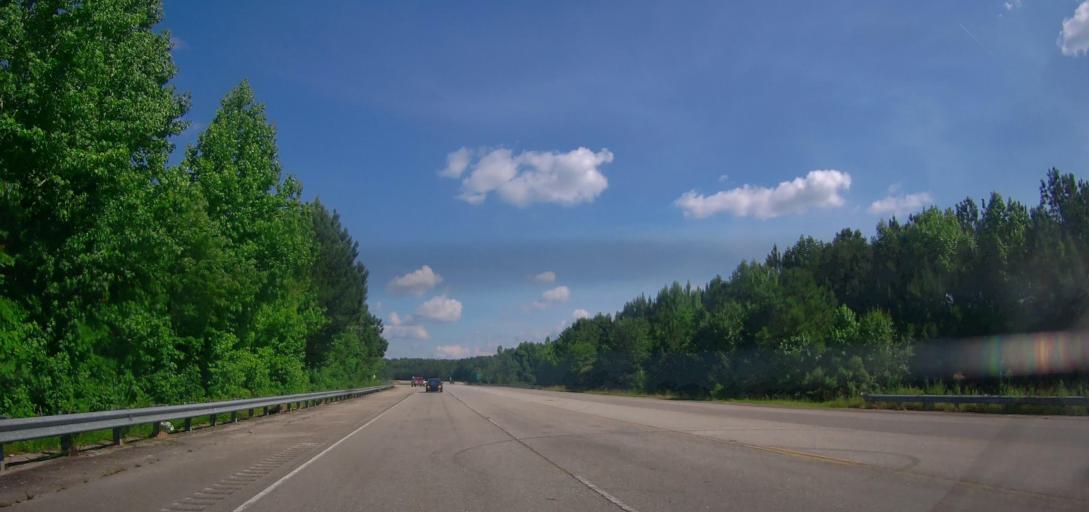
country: US
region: Georgia
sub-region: Henry County
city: Hampton
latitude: 33.3745
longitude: -84.3070
